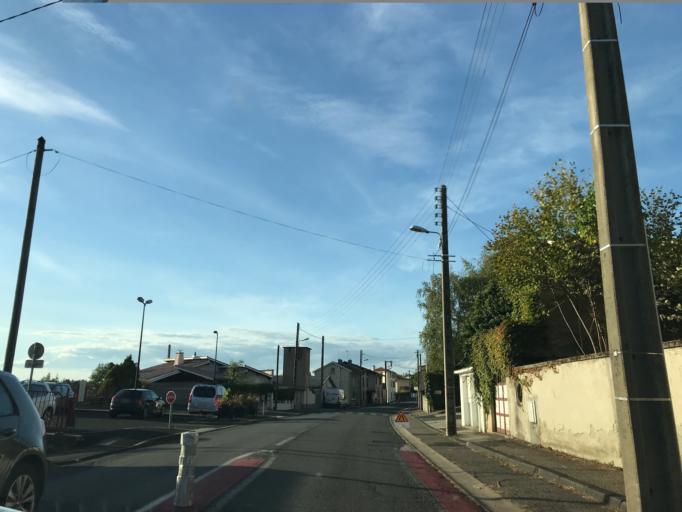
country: FR
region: Auvergne
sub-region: Departement du Puy-de-Dome
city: Thiers
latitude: 45.8609
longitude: 3.5361
